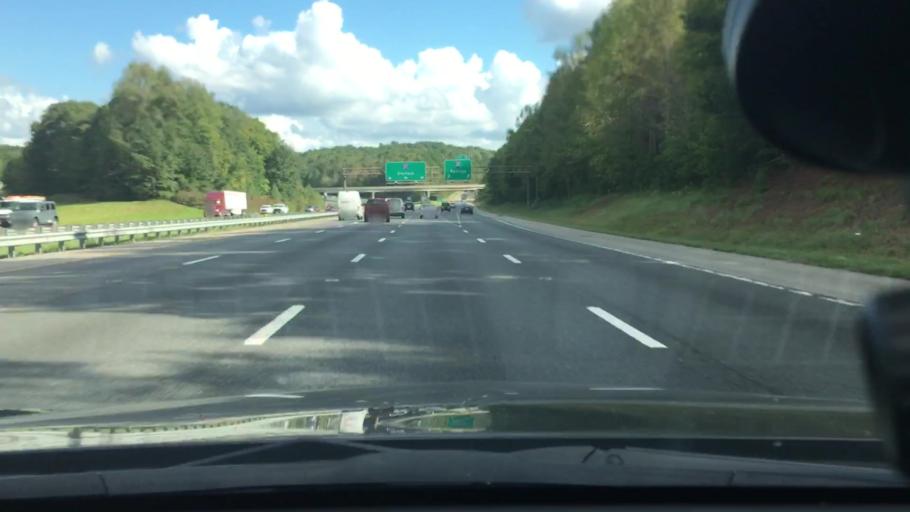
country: US
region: North Carolina
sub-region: Orange County
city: Hillsborough
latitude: 36.0613
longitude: -79.1346
